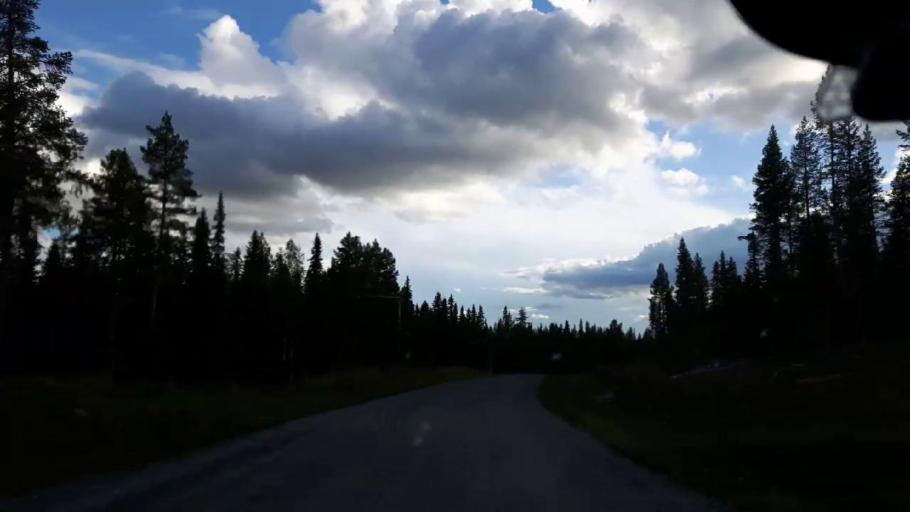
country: SE
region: Jaemtland
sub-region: Stroemsunds Kommun
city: Stroemsund
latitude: 63.3365
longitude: 15.5690
